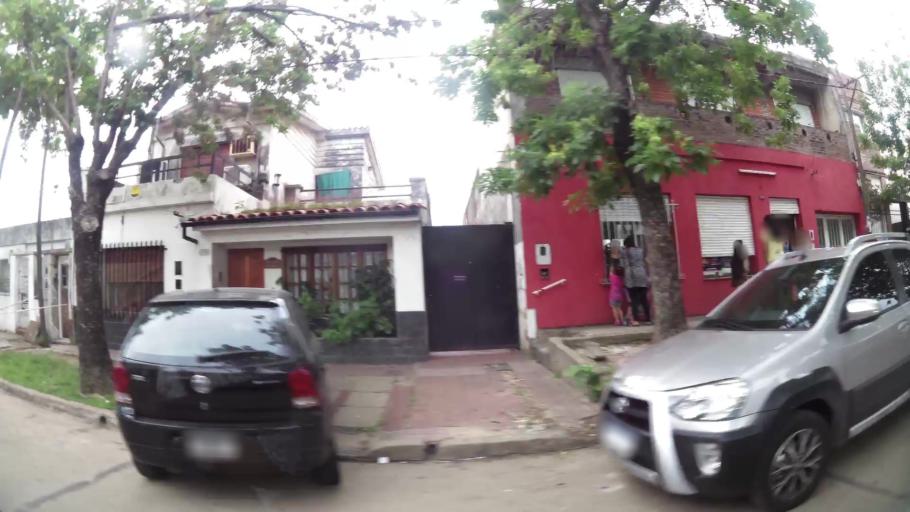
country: AR
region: Santa Fe
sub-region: Departamento de Rosario
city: Rosario
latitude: -32.9132
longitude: -60.6897
